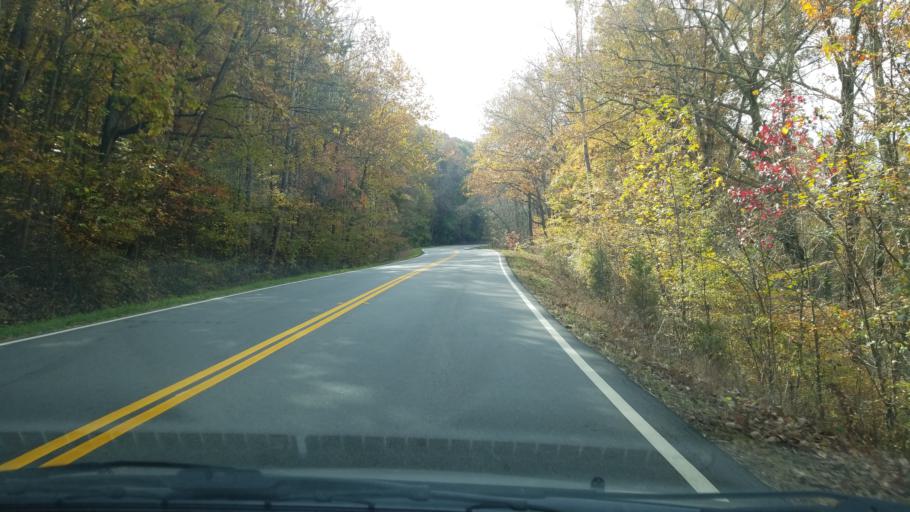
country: US
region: Georgia
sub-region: Dade County
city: Trenton
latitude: 34.8486
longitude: -85.4989
